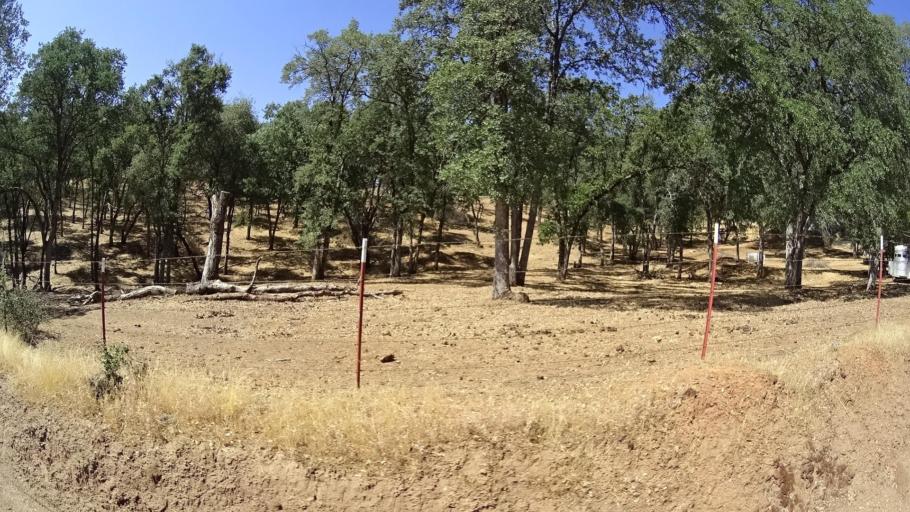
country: US
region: California
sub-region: Mariposa County
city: Mariposa
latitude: 37.4723
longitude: -119.9208
